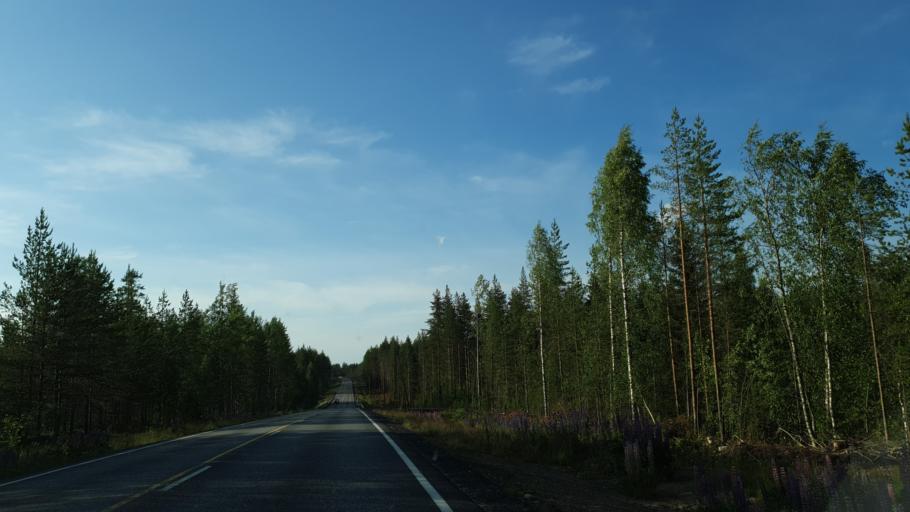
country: FI
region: Kainuu
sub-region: Kehys-Kainuu
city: Kuhmo
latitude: 64.0851
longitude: 29.4837
